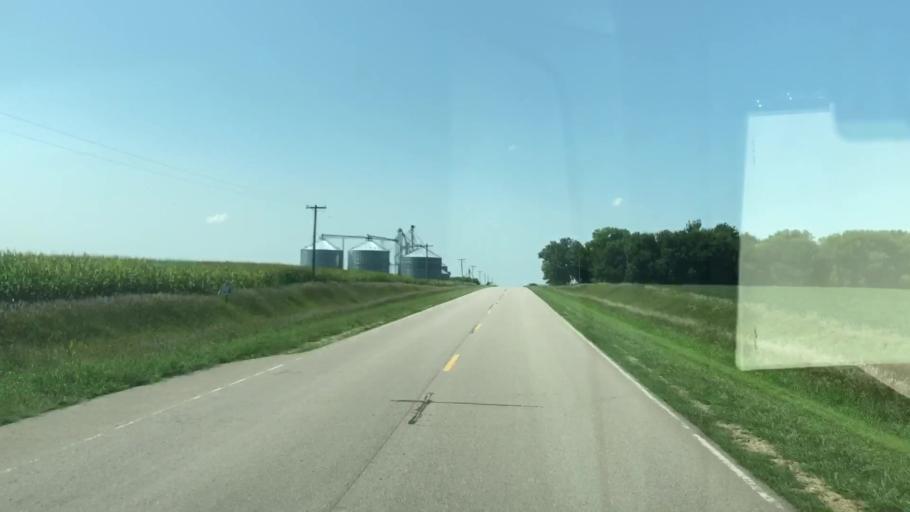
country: US
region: Iowa
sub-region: O'Brien County
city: Sheldon
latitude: 43.2443
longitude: -95.7687
